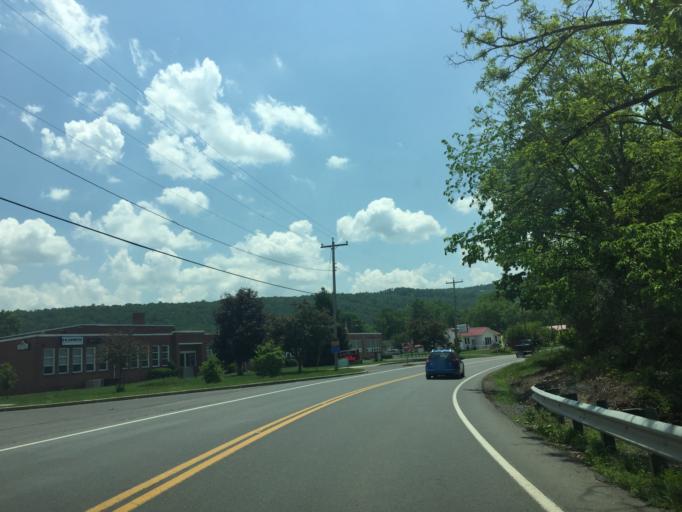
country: US
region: Virginia
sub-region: Shenandoah County
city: Woodstock
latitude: 39.0813
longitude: -78.5918
